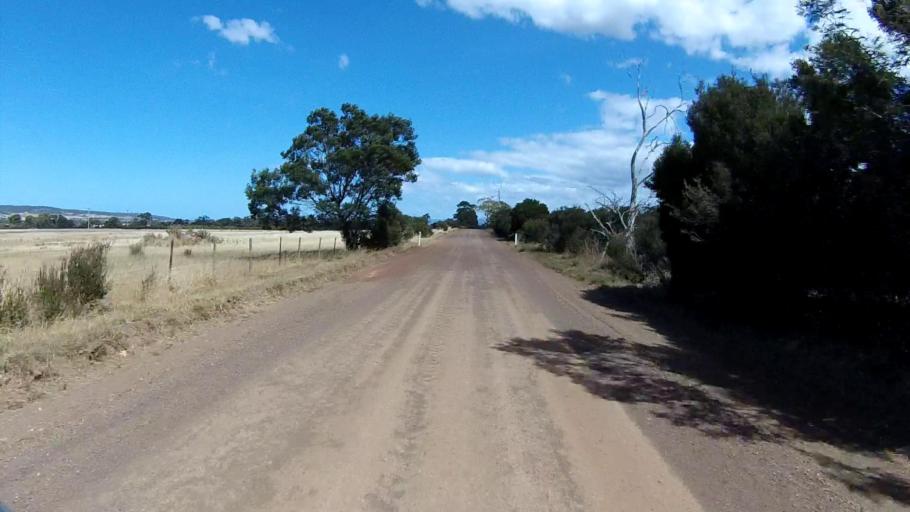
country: AU
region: Tasmania
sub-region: Break O'Day
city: St Helens
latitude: -41.9750
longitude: 148.0716
